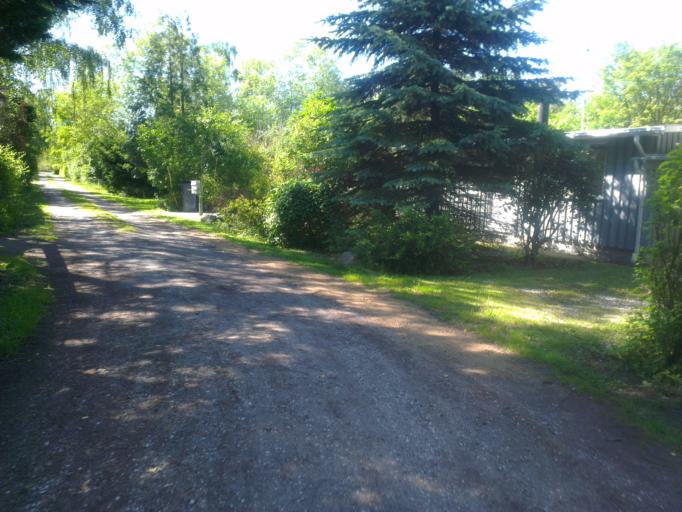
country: DK
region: Capital Region
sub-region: Halsnaes Kommune
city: Liseleje
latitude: 55.9318
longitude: 11.9435
